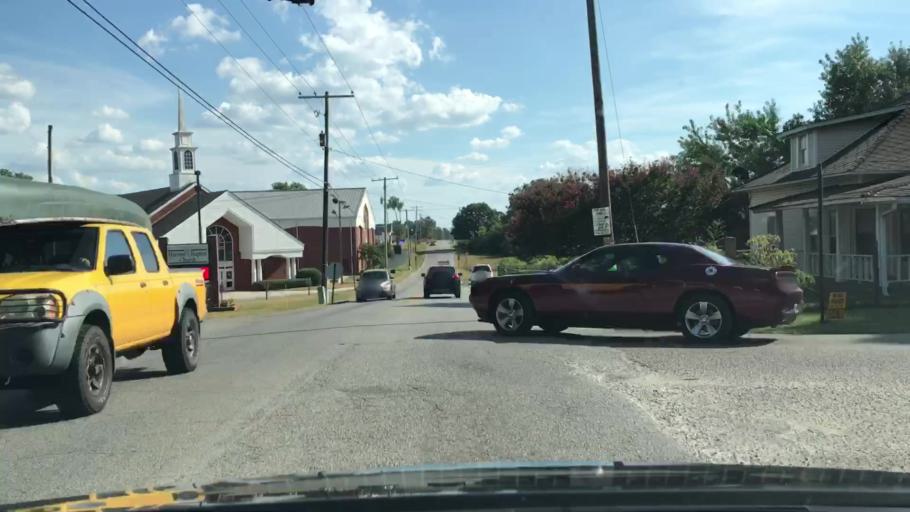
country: US
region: Alabama
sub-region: Madison County
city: Harvest
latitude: 34.8550
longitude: -86.7491
